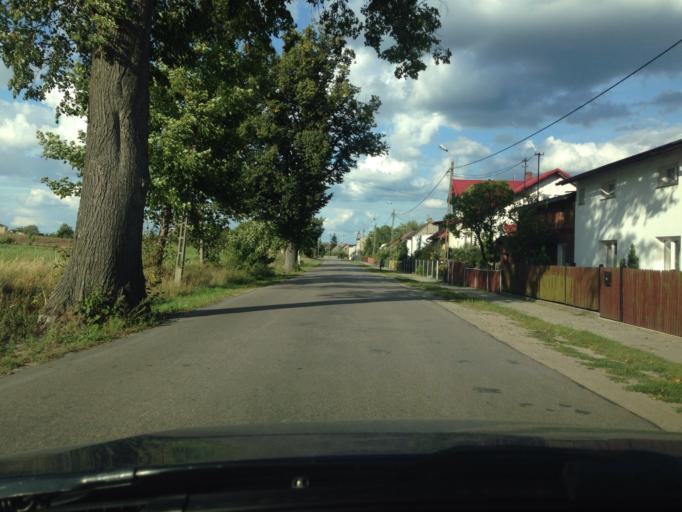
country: PL
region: Kujawsko-Pomorskie
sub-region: Powiat brodnicki
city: Gorzno
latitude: 53.1919
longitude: 19.6424
